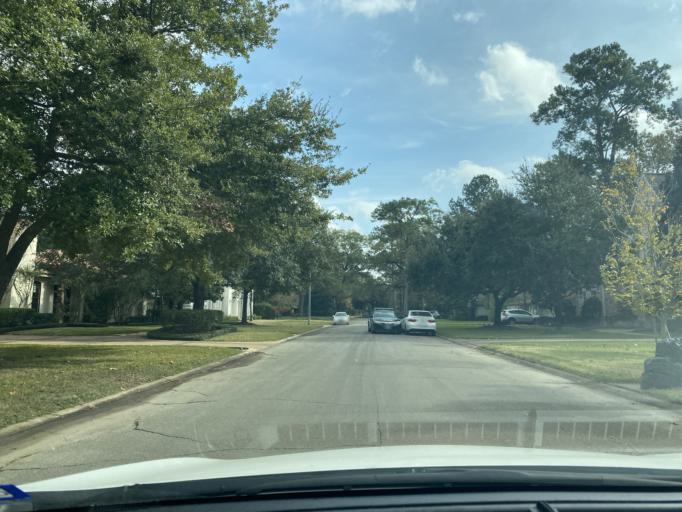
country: US
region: Texas
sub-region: Harris County
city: Hunters Creek Village
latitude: 29.7644
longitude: -95.4707
